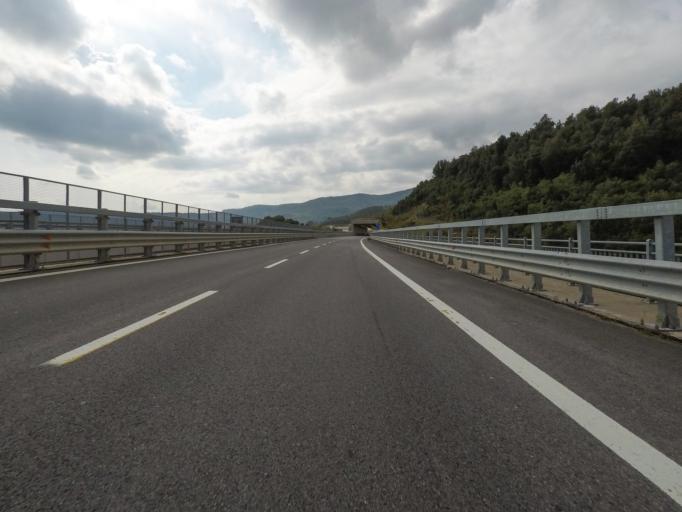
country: IT
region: Tuscany
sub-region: Provincia di Grosseto
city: Civitella Marittima
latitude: 43.0931
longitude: 11.2985
